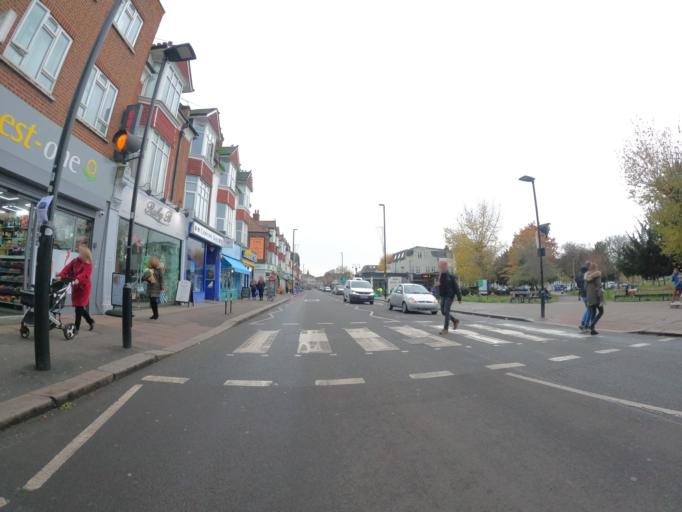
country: GB
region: England
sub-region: Greater London
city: Acton
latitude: 51.4950
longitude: -0.2552
